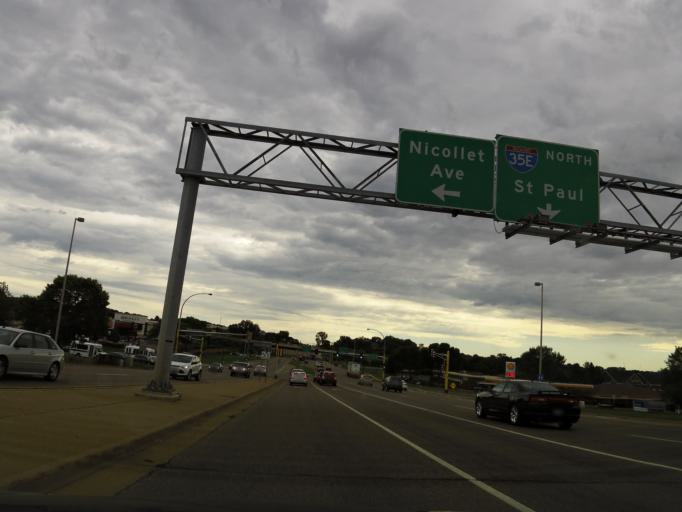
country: US
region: Minnesota
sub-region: Dakota County
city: Burnsville
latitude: 44.7450
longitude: -93.2816
